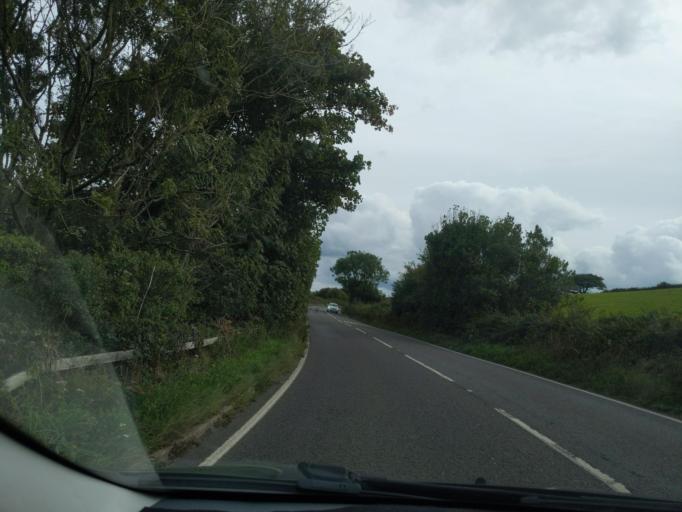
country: GB
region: England
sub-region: Cornwall
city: Mevagissey
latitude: 50.2859
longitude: -4.7875
